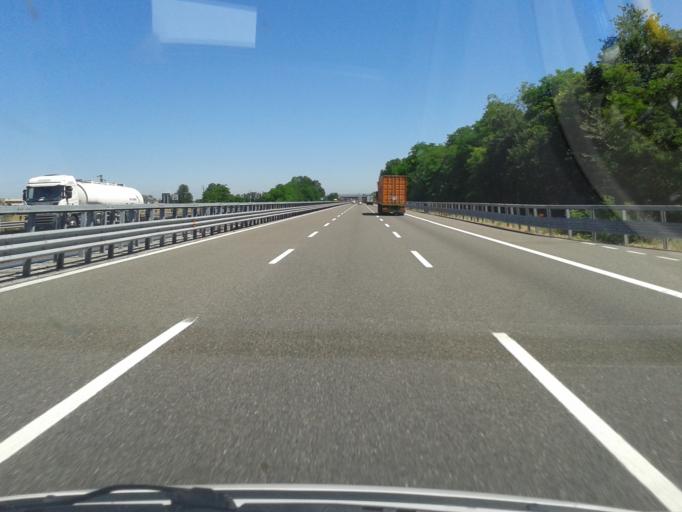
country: IT
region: Piedmont
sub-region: Provincia di Alessandria
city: Tortona
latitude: 44.8779
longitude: 8.8351
